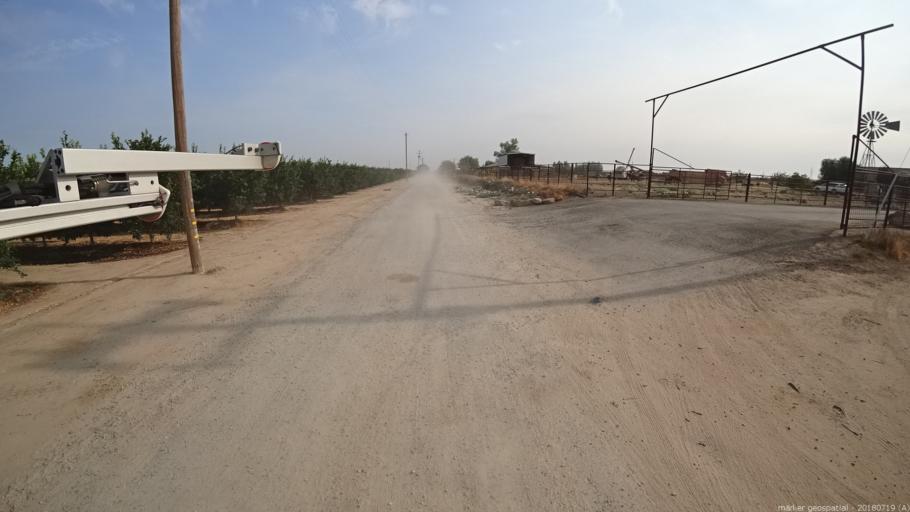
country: US
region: California
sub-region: Madera County
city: Fairmead
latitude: 37.1036
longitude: -120.1931
